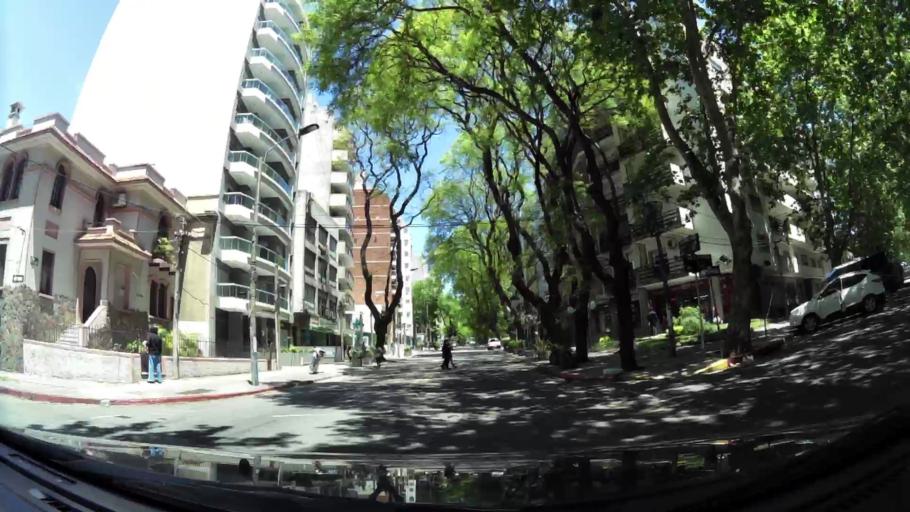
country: UY
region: Montevideo
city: Montevideo
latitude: -34.9150
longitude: -56.1537
